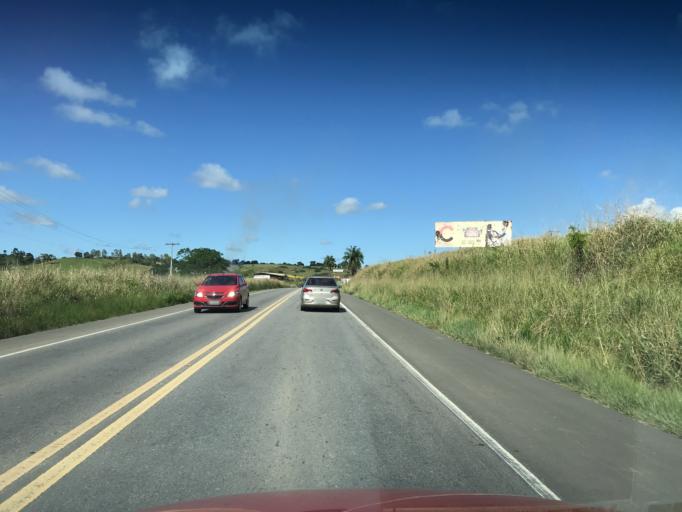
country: BR
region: Bahia
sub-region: Conceicao Do Almeida
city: Muritiba
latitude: -12.9424
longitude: -39.2515
